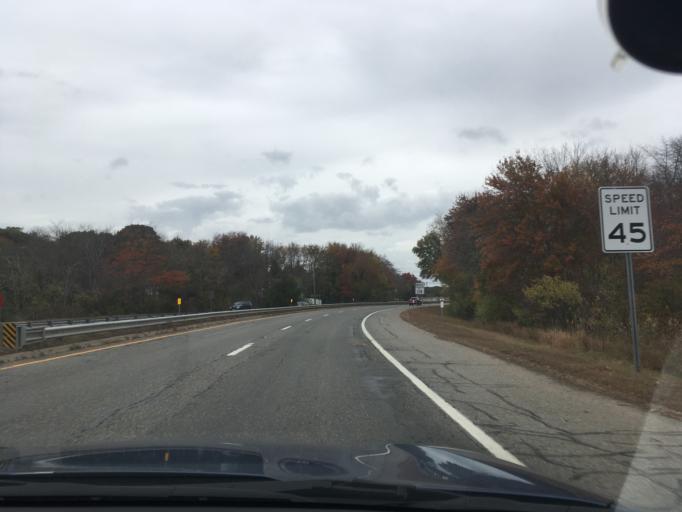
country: US
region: Rhode Island
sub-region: Bristol County
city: Barrington
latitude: 41.7591
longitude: -71.3248
